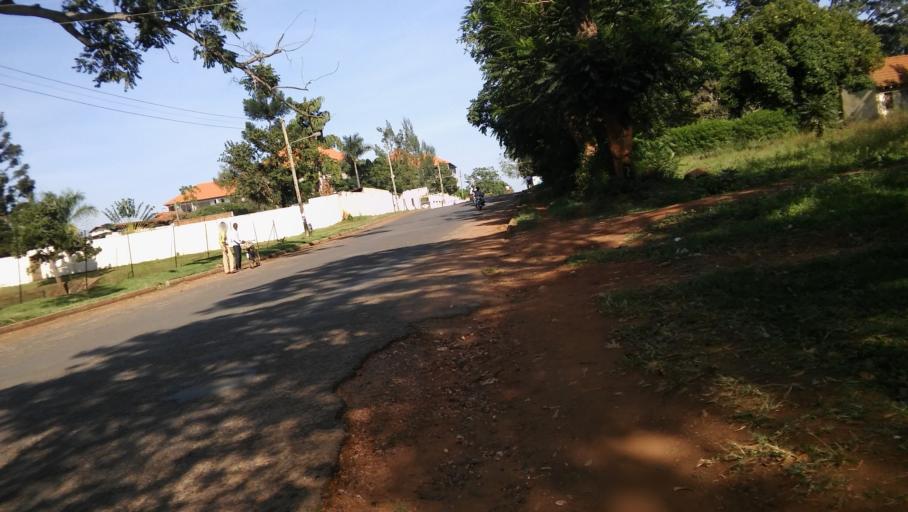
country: UG
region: Eastern Region
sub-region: Mbale District
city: Mbale
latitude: 1.0683
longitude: 34.1867
